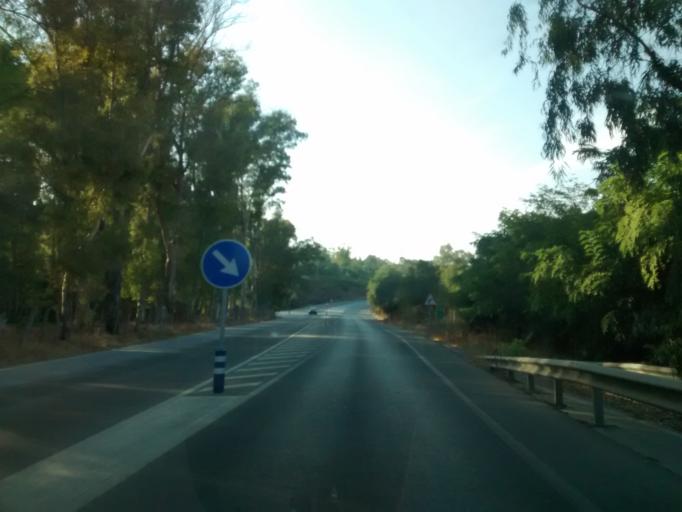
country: ES
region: Andalusia
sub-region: Provincia de Cadiz
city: Vejer de la Frontera
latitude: 36.2191
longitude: -5.9468
